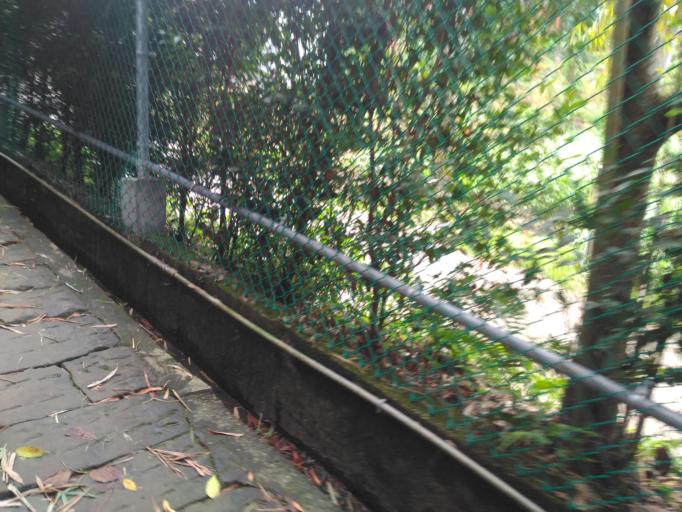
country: TW
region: Taipei
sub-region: Taipei
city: Banqiao
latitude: 24.9557
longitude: 121.4442
